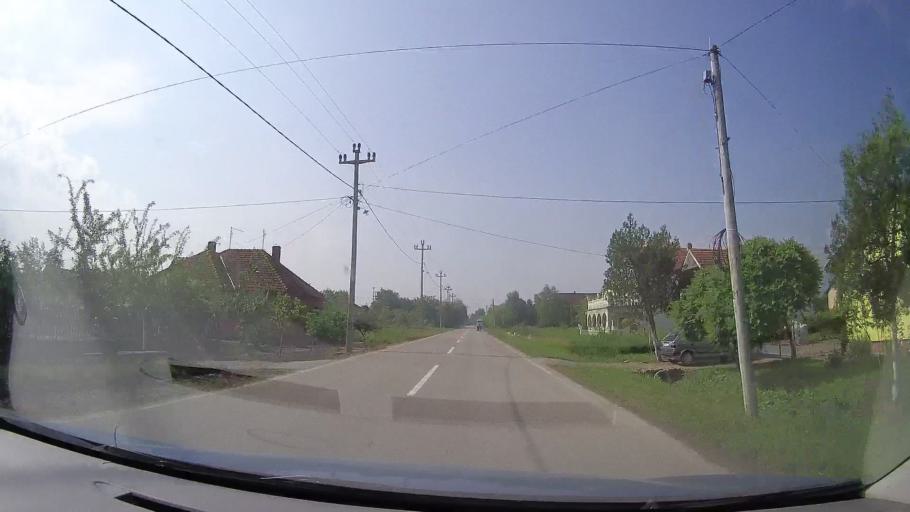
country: RS
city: Jasa Tomic
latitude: 45.4531
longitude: 20.8554
